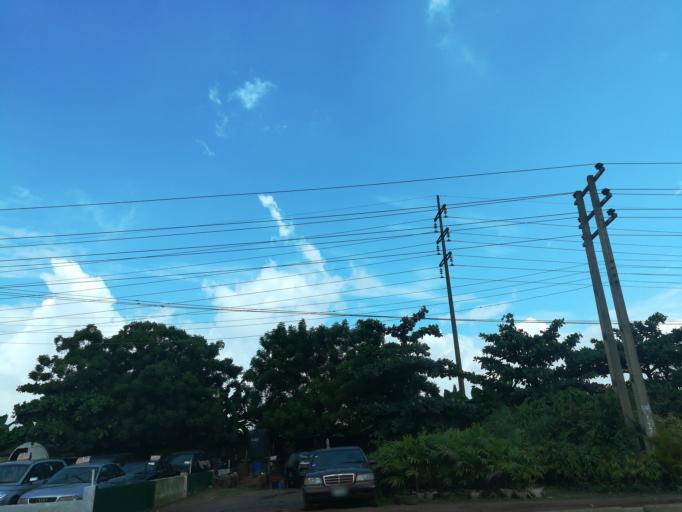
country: NG
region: Lagos
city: Ikorodu
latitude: 6.6561
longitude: 3.5196
